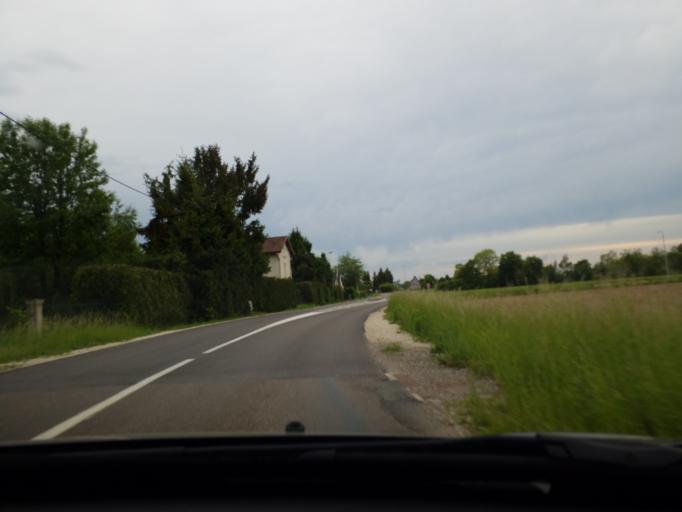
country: FR
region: Franche-Comte
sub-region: Departement de la Haute-Saone
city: Corbenay
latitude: 47.8822
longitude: 6.3101
